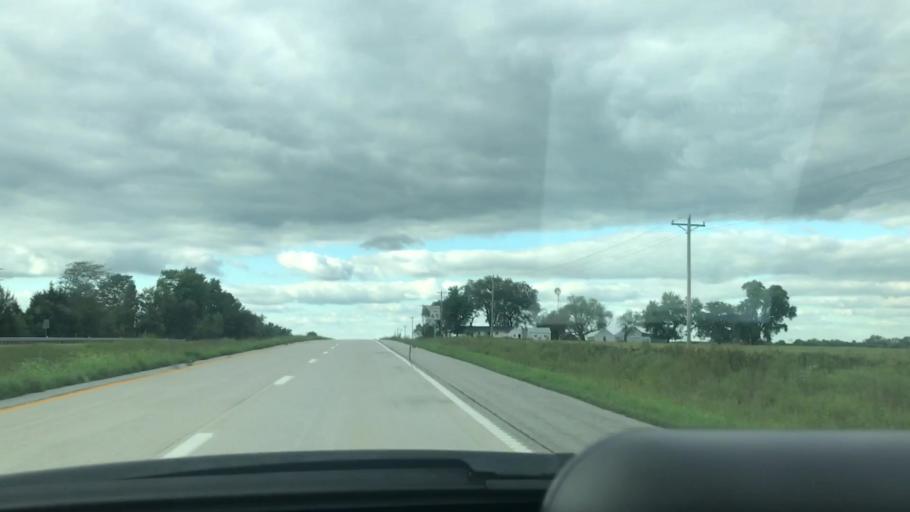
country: US
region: Missouri
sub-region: Benton County
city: Lincoln
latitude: 38.3671
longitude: -93.3388
